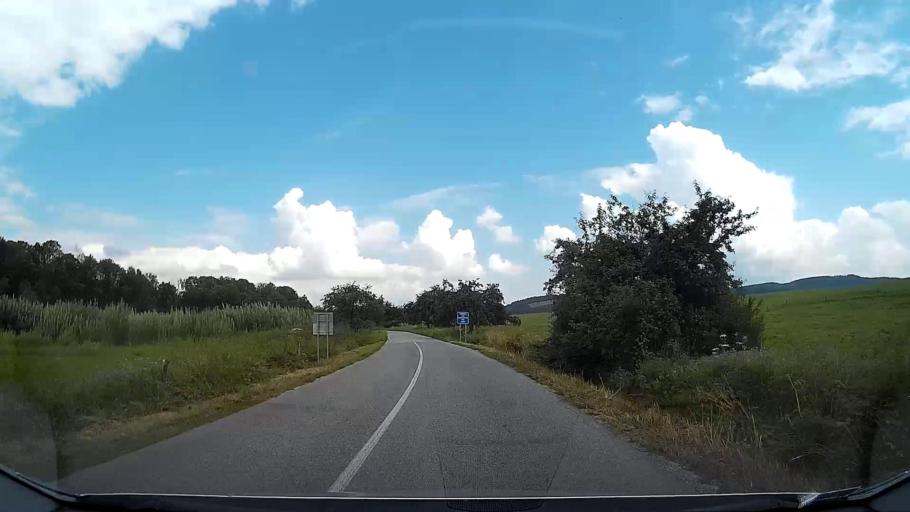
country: SK
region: Presovsky
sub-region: Okres Poprad
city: Poprad
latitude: 48.9877
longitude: 20.3867
